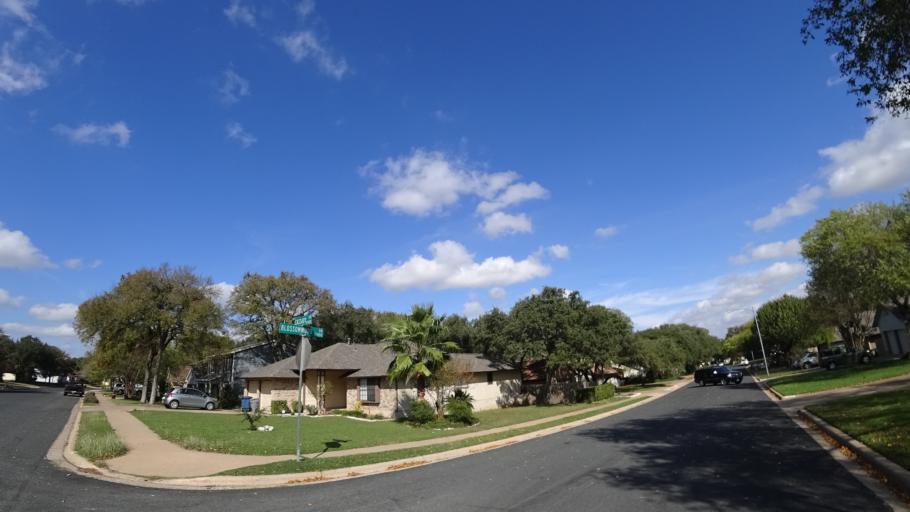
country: US
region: Texas
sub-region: Travis County
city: Wells Branch
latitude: 30.4221
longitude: -97.7209
